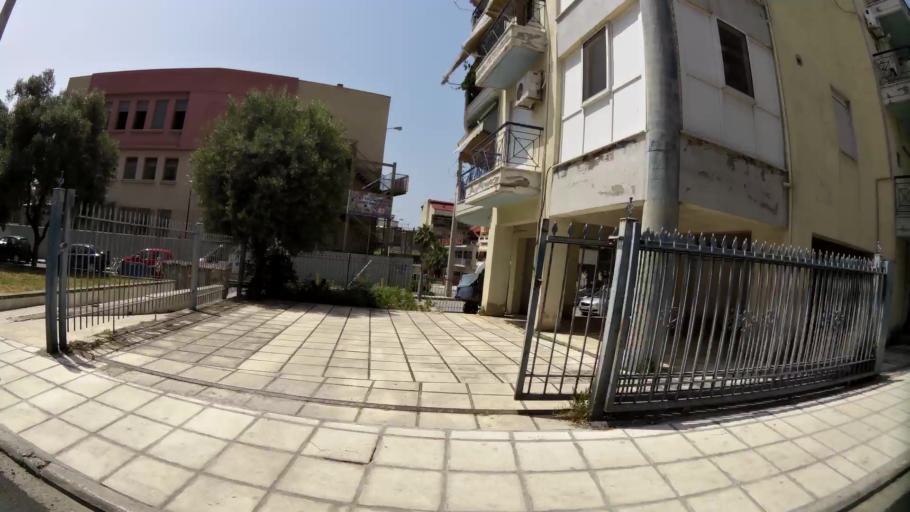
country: GR
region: Central Macedonia
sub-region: Nomos Thessalonikis
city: Evosmos
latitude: 40.6722
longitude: 22.8987
